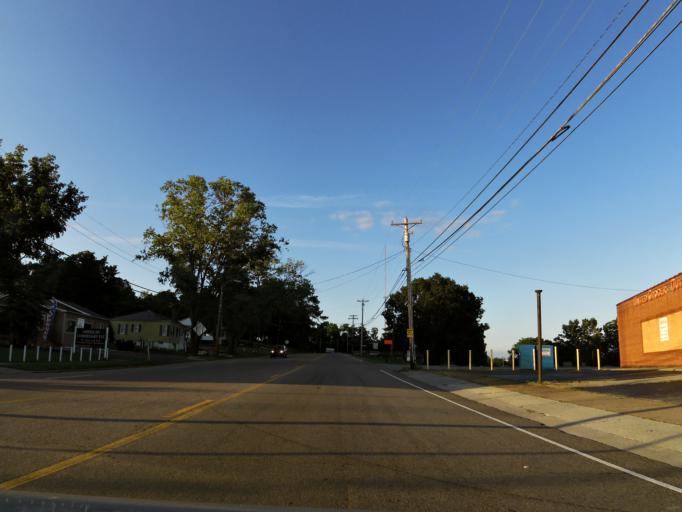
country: US
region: Tennessee
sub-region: Loudon County
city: Lenoir City
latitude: 35.7991
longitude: -84.2550
